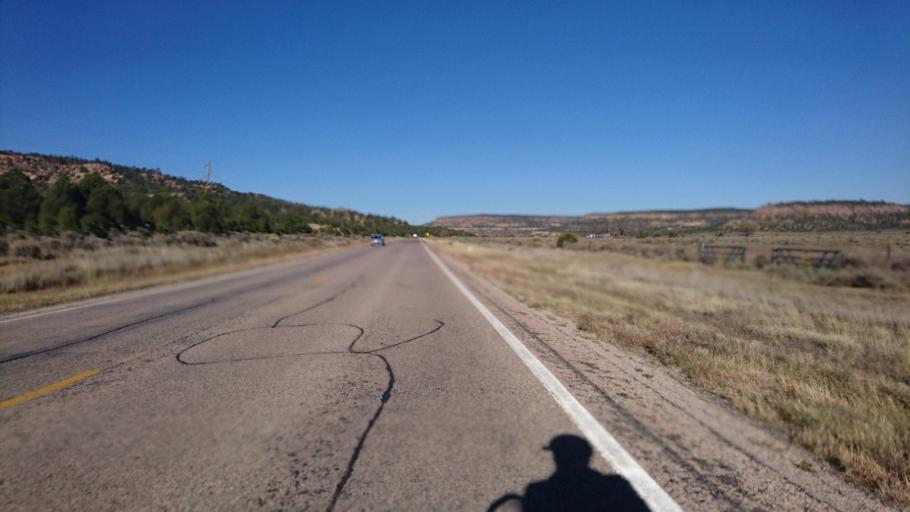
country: US
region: New Mexico
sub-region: McKinley County
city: Black Rock
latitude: 35.1128
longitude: -108.6038
